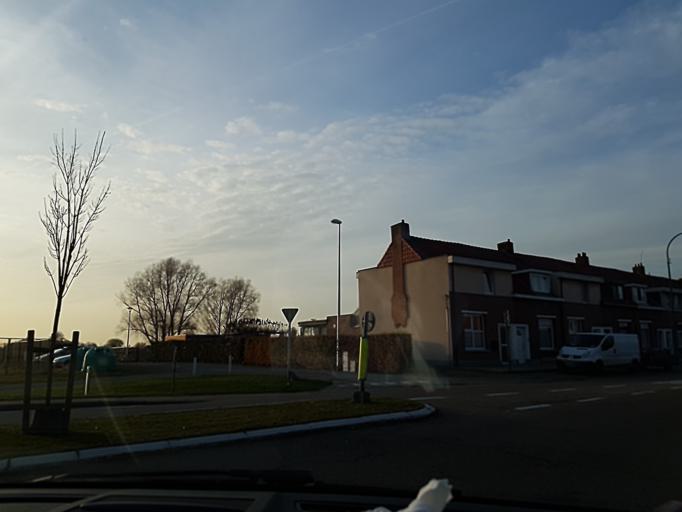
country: BE
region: Flanders
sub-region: Provincie Antwerpen
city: Essen
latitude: 51.4613
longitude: 4.4750
